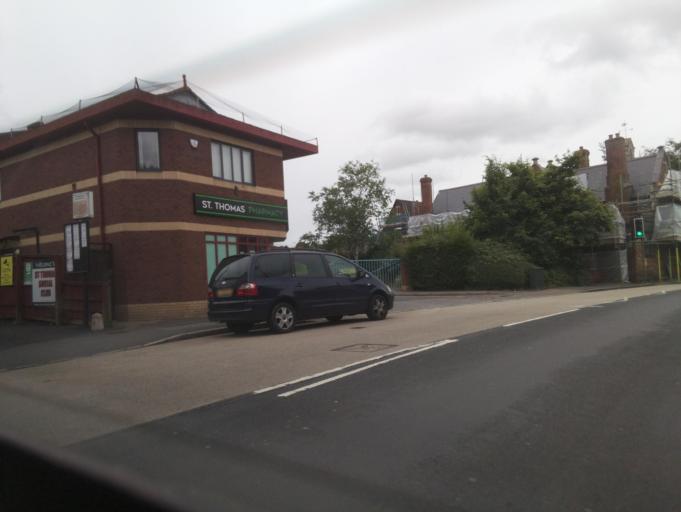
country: GB
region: England
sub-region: Devon
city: Exeter
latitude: 50.7148
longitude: -3.5451
